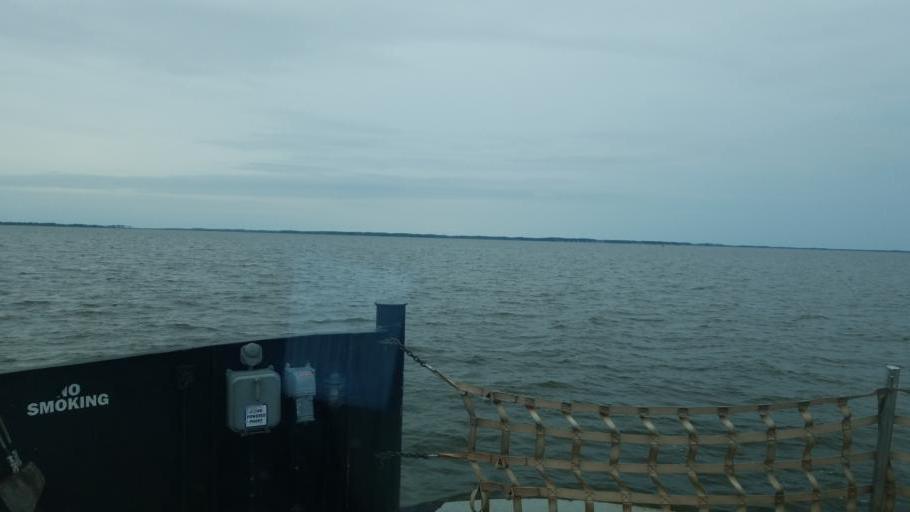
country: US
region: North Carolina
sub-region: Currituck County
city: Currituck
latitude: 36.4573
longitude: -75.9832
